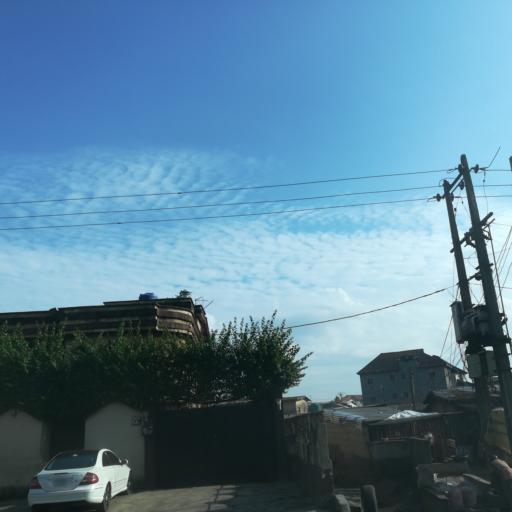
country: NG
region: Lagos
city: Agege
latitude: 6.6150
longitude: 3.3253
